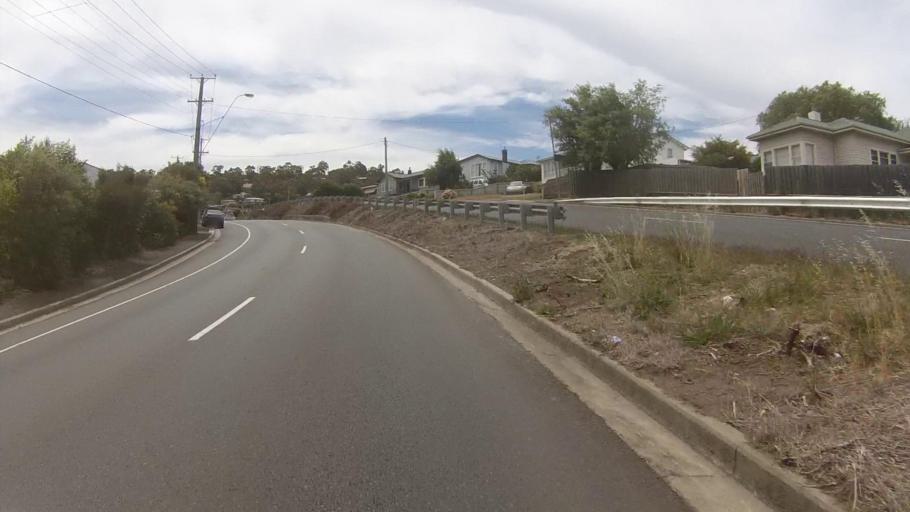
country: AU
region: Tasmania
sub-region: Clarence
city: Lindisfarne
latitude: -42.8501
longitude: 147.3624
